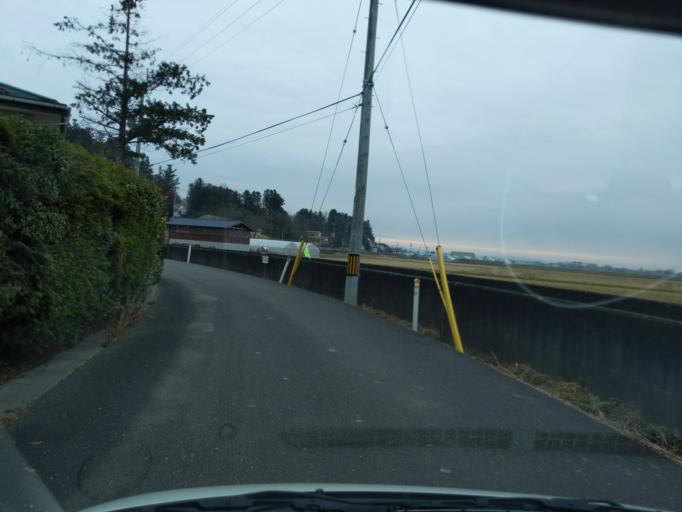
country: JP
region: Iwate
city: Ichinoseki
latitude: 38.7387
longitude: 141.2475
